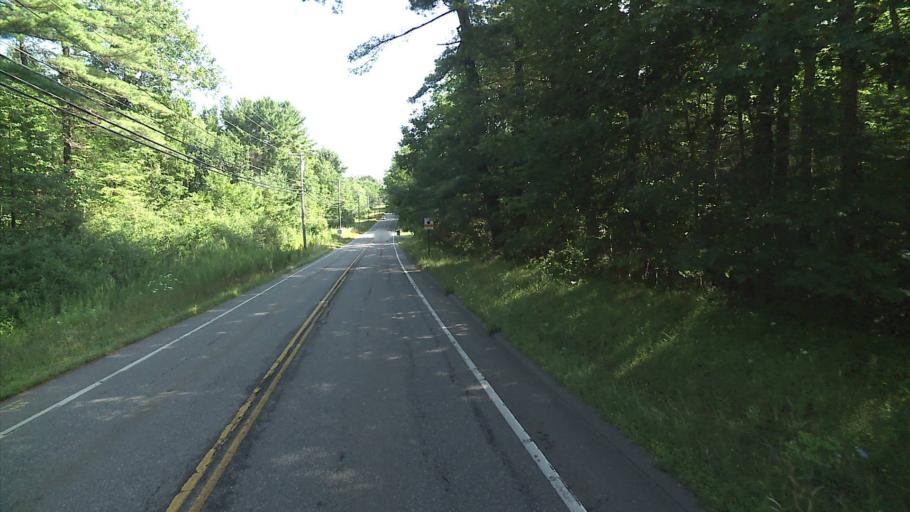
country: US
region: Connecticut
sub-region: Litchfield County
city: Winsted
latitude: 41.8624
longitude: -73.0703
